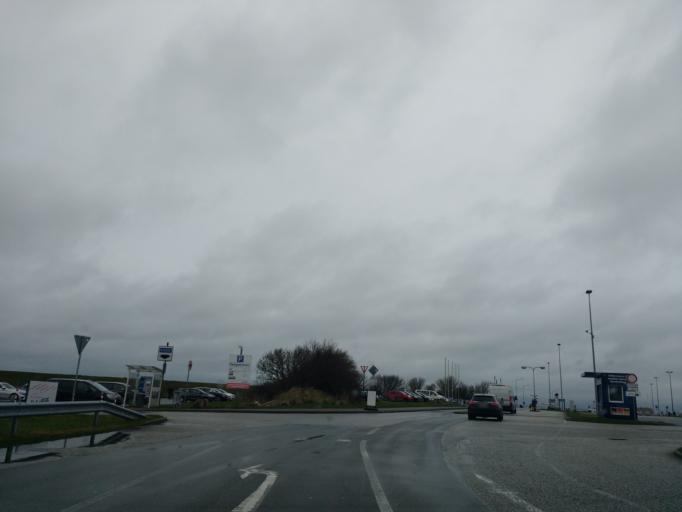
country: DE
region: Schleswig-Holstein
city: Fehmarn
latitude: 54.5024
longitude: 11.2235
